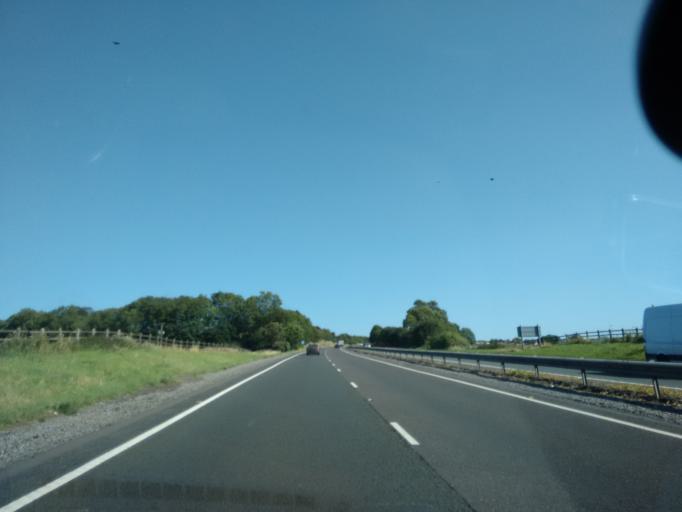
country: GB
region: England
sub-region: Northumberland
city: Corbridge
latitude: 54.9837
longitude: -2.0116
